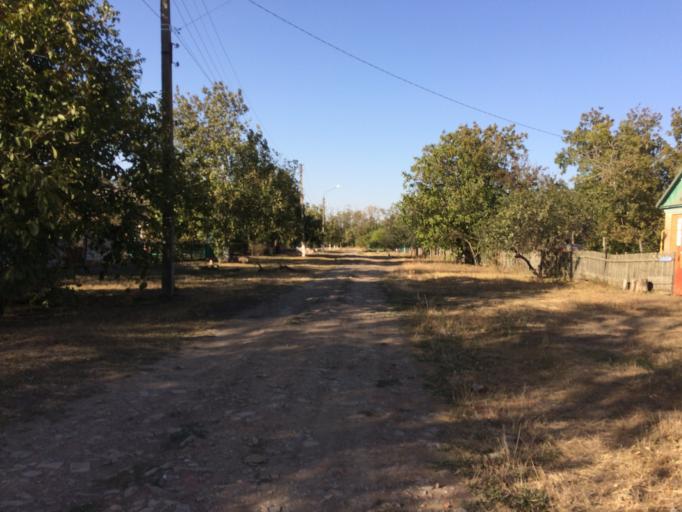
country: RU
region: Rostov
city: Gigant
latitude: 46.5250
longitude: 41.1882
